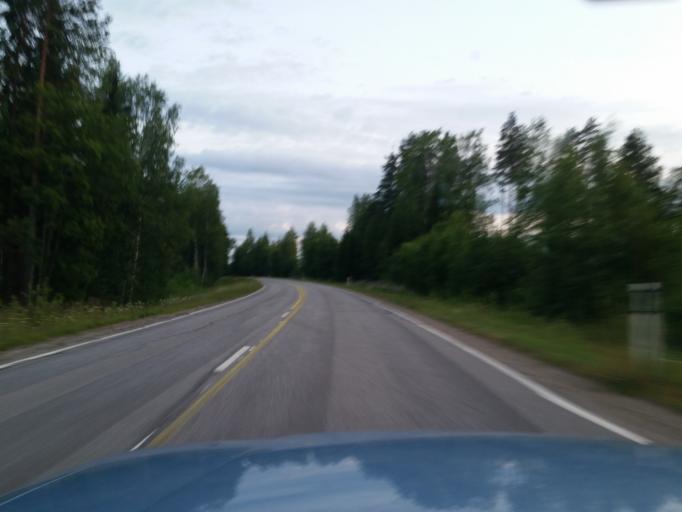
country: FI
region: Southern Savonia
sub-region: Savonlinna
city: Sulkava
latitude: 61.8295
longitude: 28.4437
